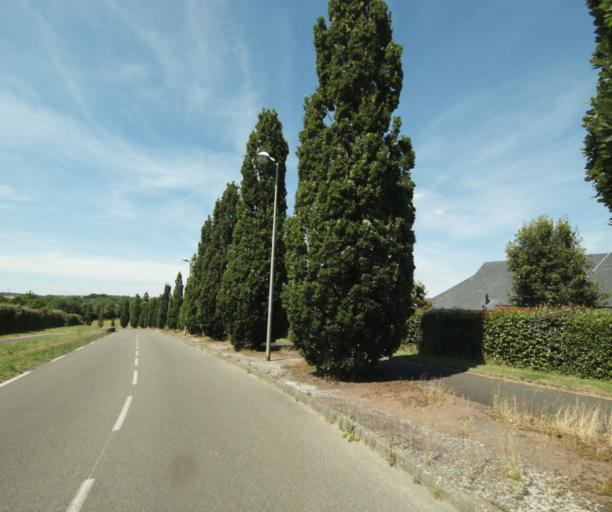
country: FR
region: Pays de la Loire
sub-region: Departement de la Mayenne
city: Change
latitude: 48.0831
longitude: -0.7835
